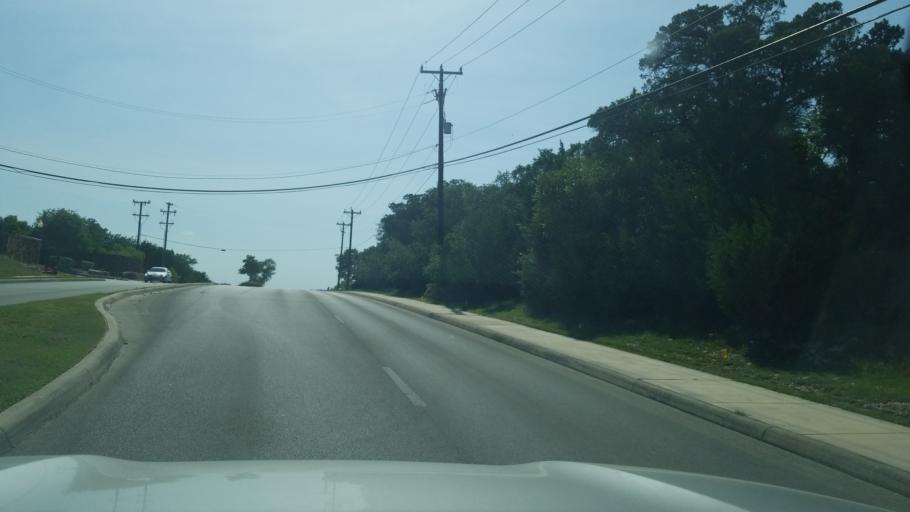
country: US
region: Texas
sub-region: Bexar County
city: Timberwood Park
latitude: 29.6682
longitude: -98.4607
